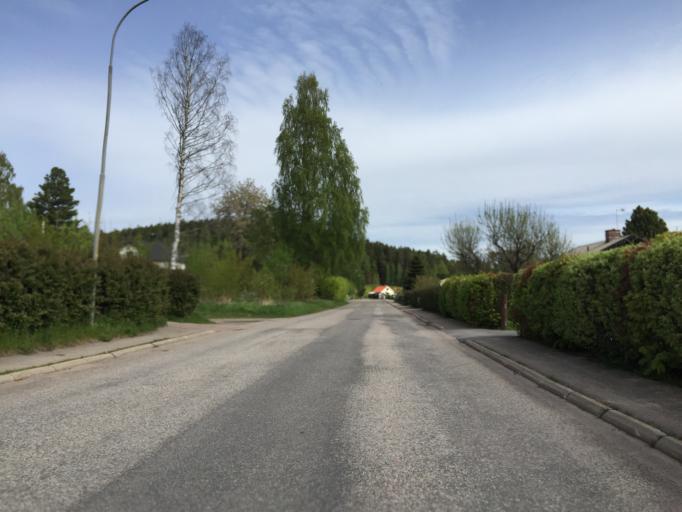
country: SE
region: Dalarna
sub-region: Ludvika Kommun
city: Ludvika
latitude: 60.1276
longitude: 15.1871
